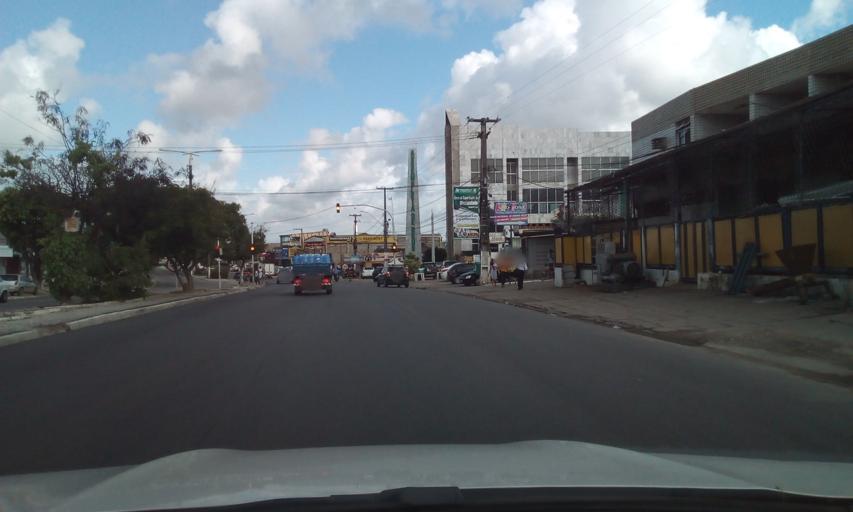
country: BR
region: Pernambuco
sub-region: Abreu E Lima
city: Abreu e Lima
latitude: -7.9089
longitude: -34.9022
